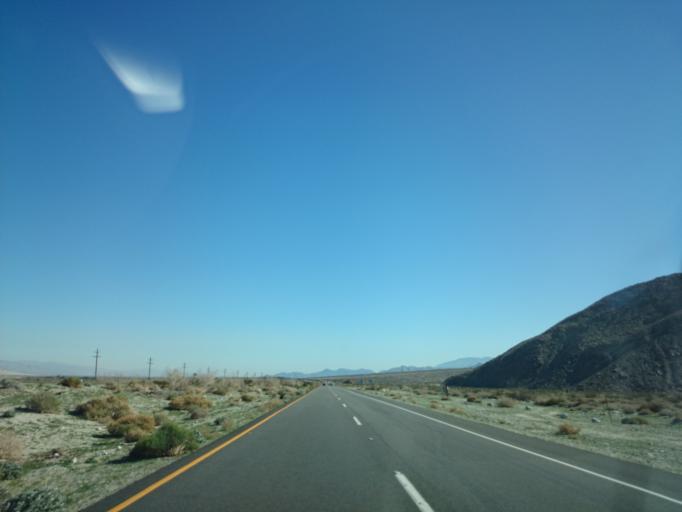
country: US
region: California
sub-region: Riverside County
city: Garnet
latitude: 33.8763
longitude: -116.5860
